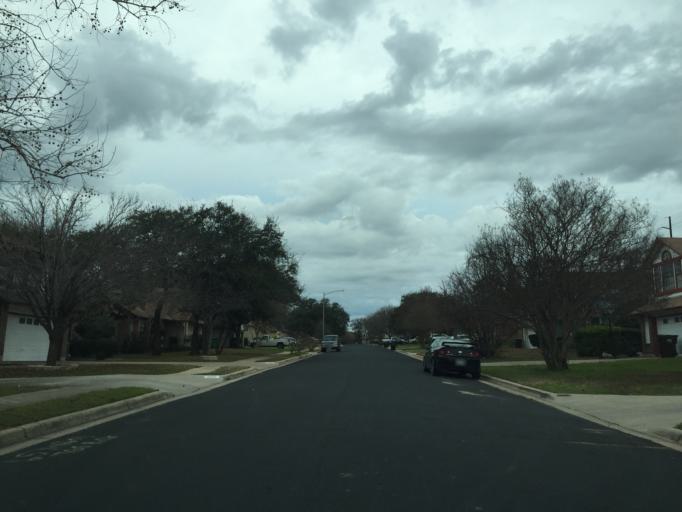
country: US
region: Texas
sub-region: Williamson County
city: Jollyville
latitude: 30.4473
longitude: -97.7454
